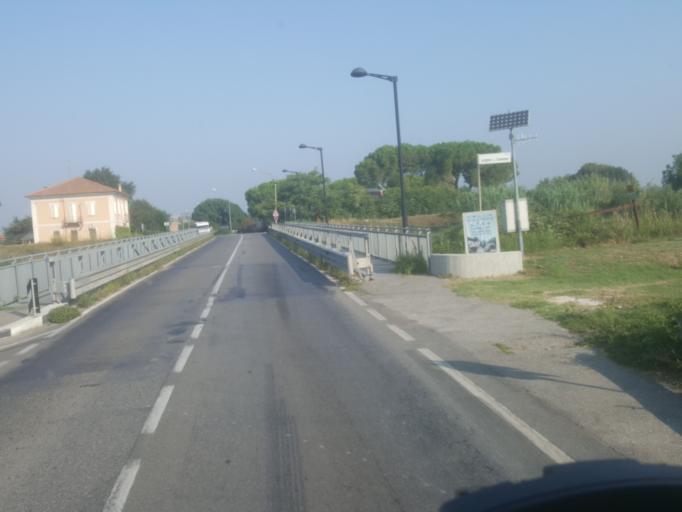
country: IT
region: Emilia-Romagna
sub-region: Provincia di Ravenna
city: Mezzano
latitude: 44.4693
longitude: 12.0833
